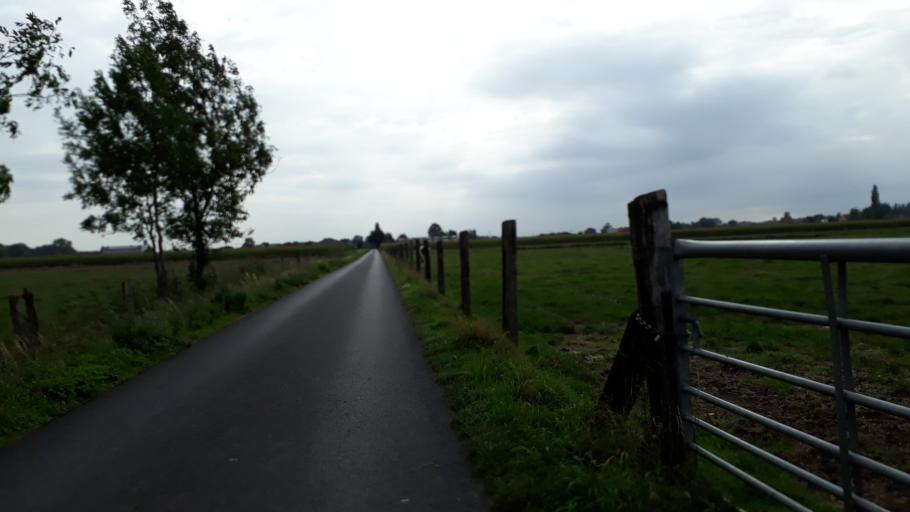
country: BE
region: Flanders
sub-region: Provincie West-Vlaanderen
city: Lichtervelde
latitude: 51.0540
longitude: 3.1335
